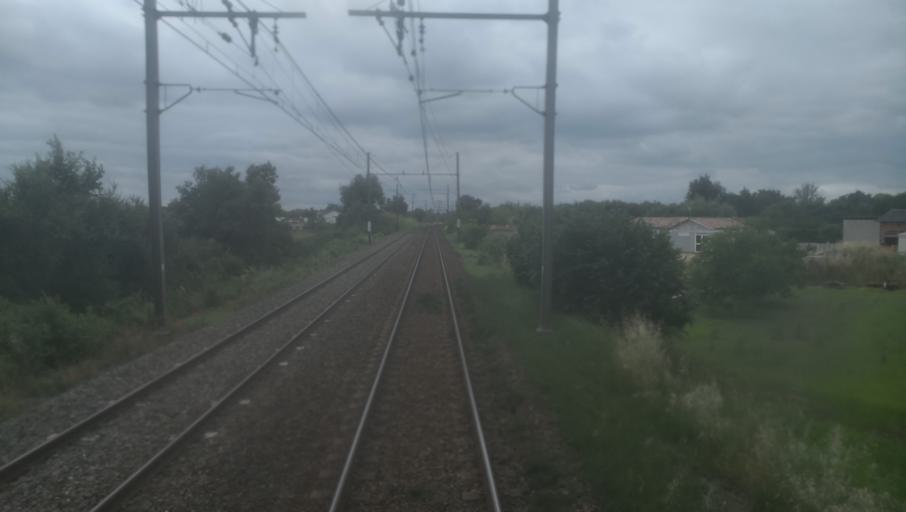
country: FR
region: Midi-Pyrenees
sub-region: Departement du Tarn-et-Garonne
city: Montbeton
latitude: 44.0149
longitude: 1.3090
